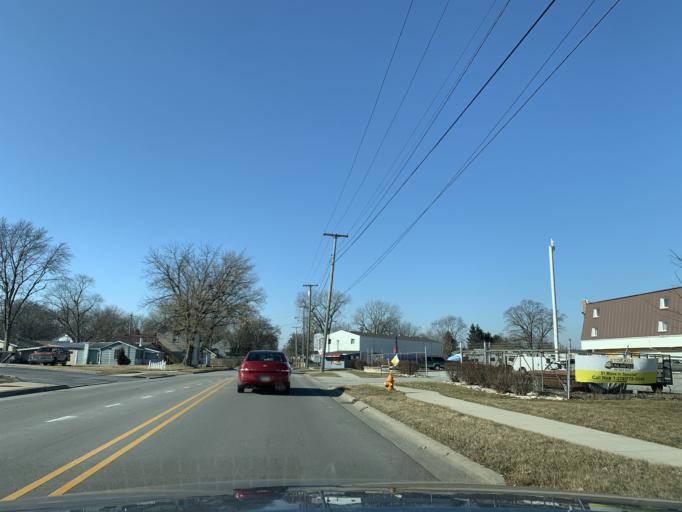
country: US
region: Indiana
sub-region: Lake County
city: Crown Point
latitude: 41.4203
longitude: -87.3554
